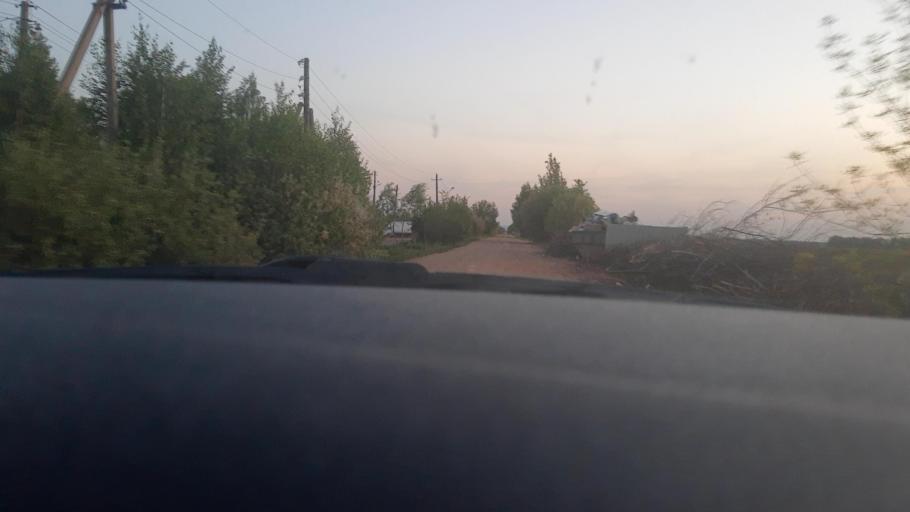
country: RU
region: Bashkortostan
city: Iglino
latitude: 54.7546
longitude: 56.3359
